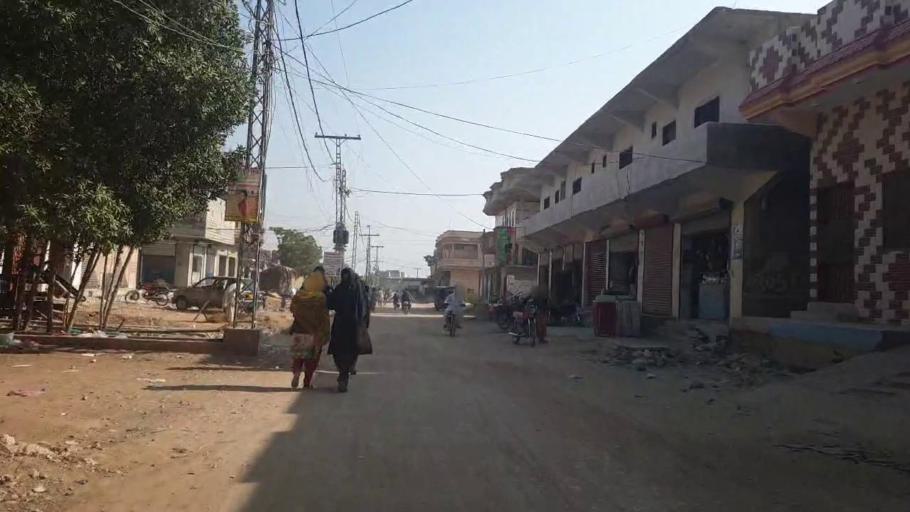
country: PK
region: Sindh
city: Jamshoro
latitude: 25.4093
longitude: 68.2787
